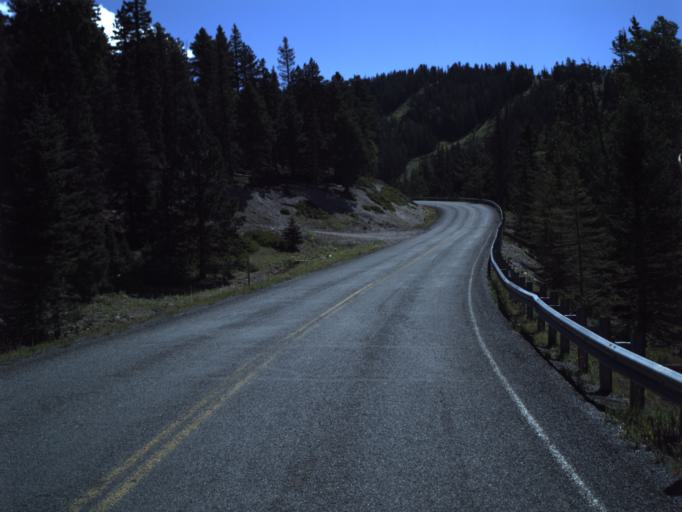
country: US
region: Utah
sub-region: Piute County
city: Junction
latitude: 38.3128
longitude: -112.3986
